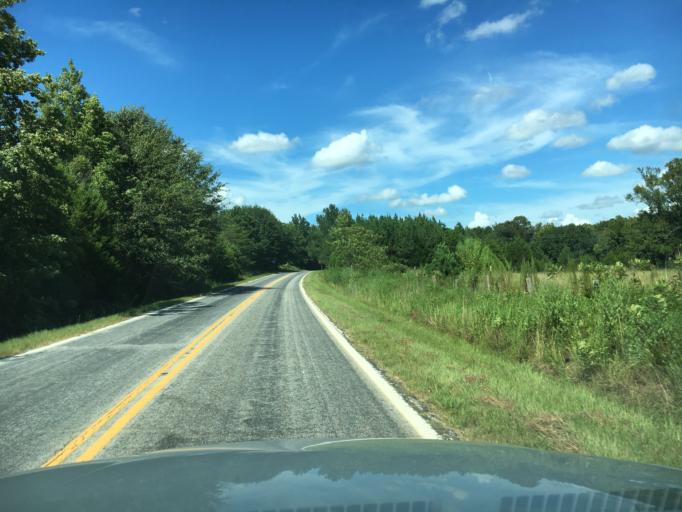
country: US
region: South Carolina
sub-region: Greenwood County
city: Ware Shoals
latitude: 34.4142
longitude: -82.2899
